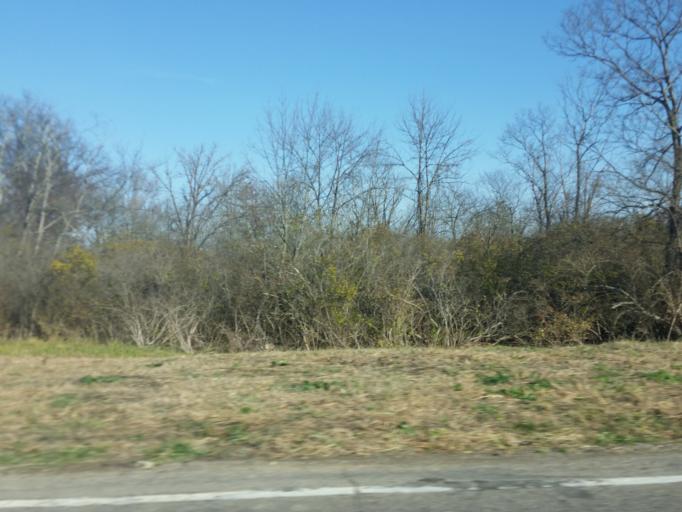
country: US
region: Ohio
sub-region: Butler County
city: Oxford
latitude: 39.4782
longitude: -84.7111
